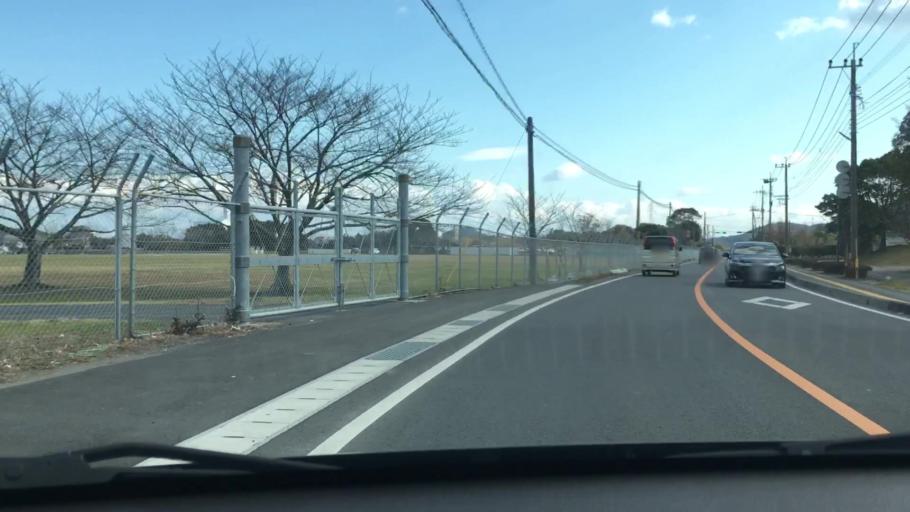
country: JP
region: Oita
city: Saiki
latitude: 32.9698
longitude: 131.9125
